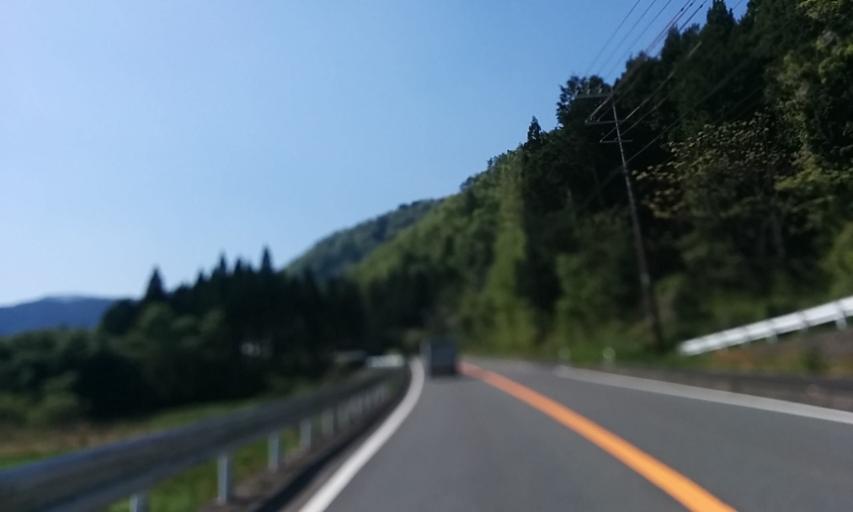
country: JP
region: Kyoto
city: Maizuru
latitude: 35.2794
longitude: 135.5409
